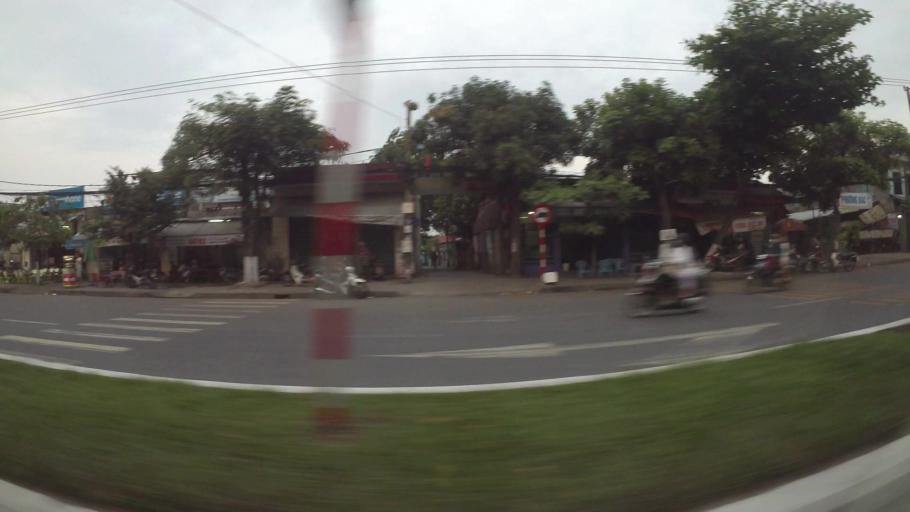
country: VN
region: Da Nang
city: Lien Chieu
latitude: 16.0831
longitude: 108.1458
